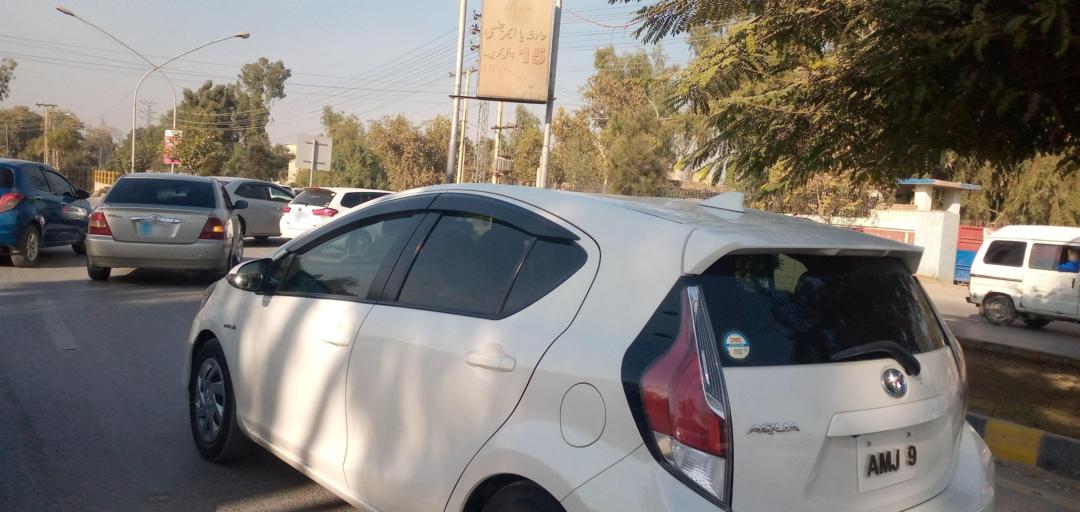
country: PK
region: Khyber Pakhtunkhwa
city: Peshawar
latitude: 33.9723
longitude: 71.4391
